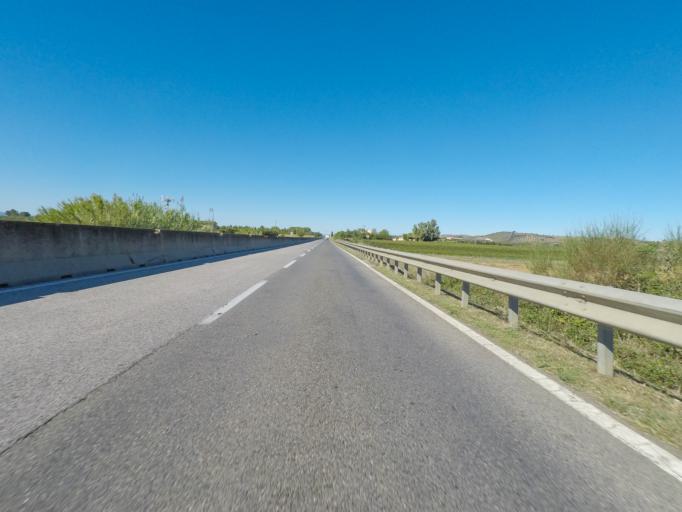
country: IT
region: Tuscany
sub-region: Provincia di Grosseto
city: Grosseto
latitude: 42.6830
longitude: 11.1398
